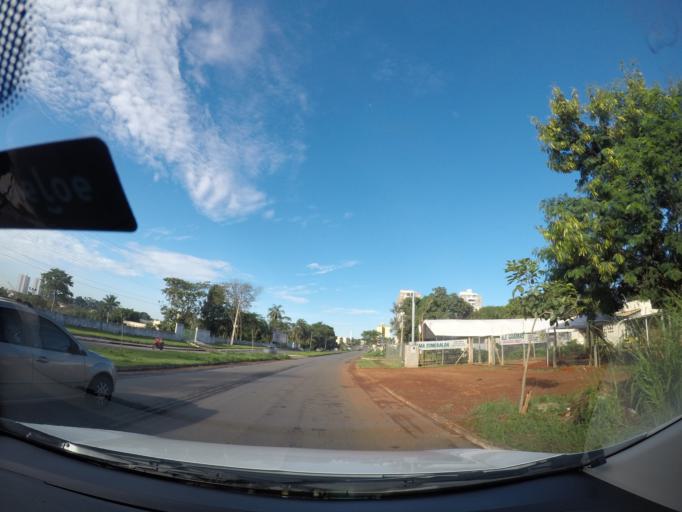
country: BR
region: Goias
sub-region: Goiania
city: Goiania
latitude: -16.7467
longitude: -49.2701
